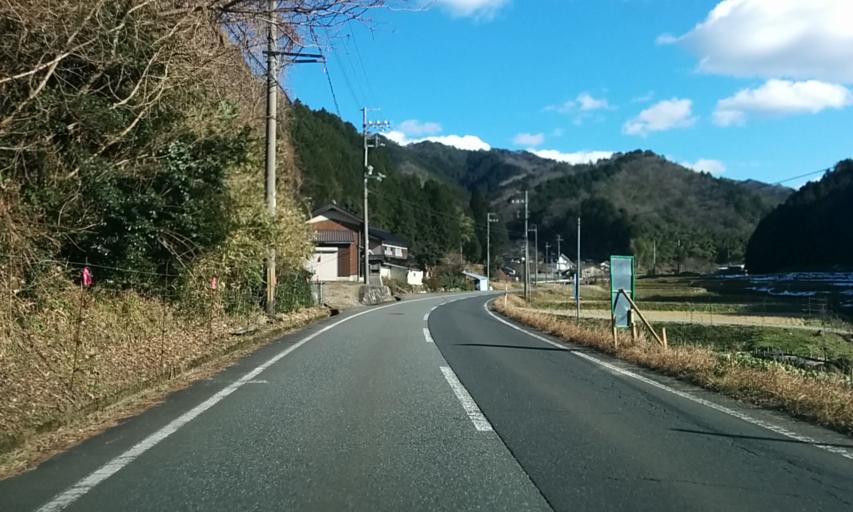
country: JP
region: Hyogo
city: Toyooka
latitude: 35.4317
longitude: 134.9548
